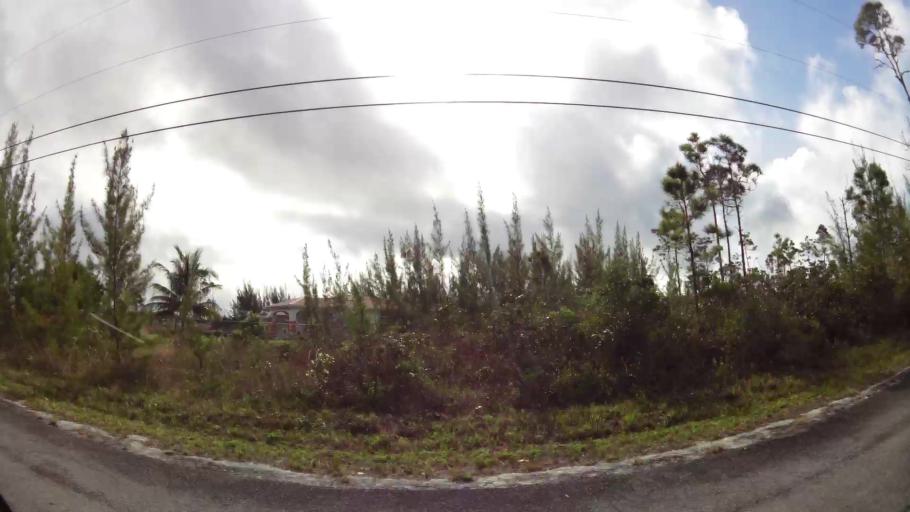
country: BS
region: Freeport
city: Lucaya
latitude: 26.5771
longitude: -78.5848
